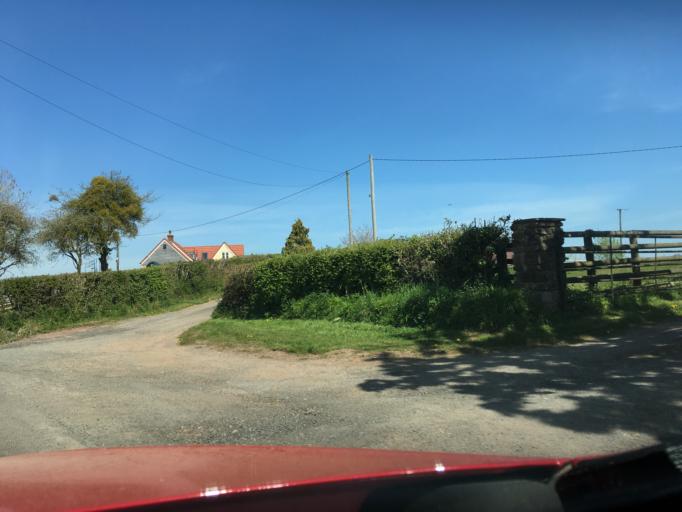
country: GB
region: Wales
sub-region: Monmouthshire
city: Llangwm
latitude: 51.7647
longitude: -2.8291
